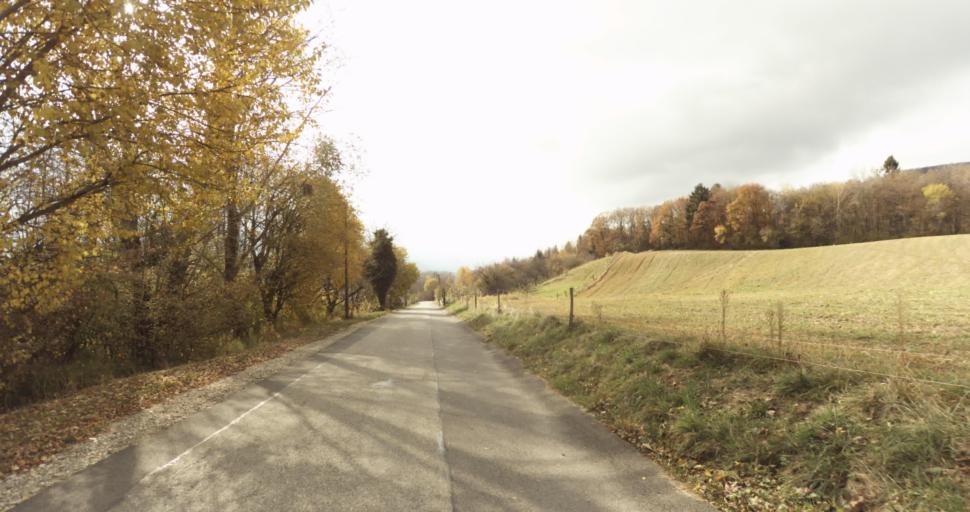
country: FR
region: Rhone-Alpes
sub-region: Departement de la Haute-Savoie
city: Epagny
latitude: 45.9557
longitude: 6.0779
